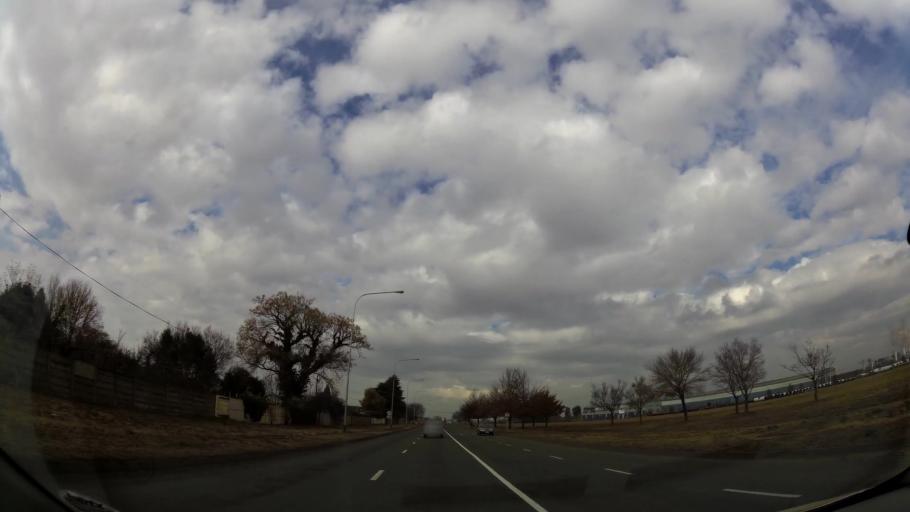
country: ZA
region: Gauteng
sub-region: Sedibeng District Municipality
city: Meyerton
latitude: -26.5712
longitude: 28.0193
